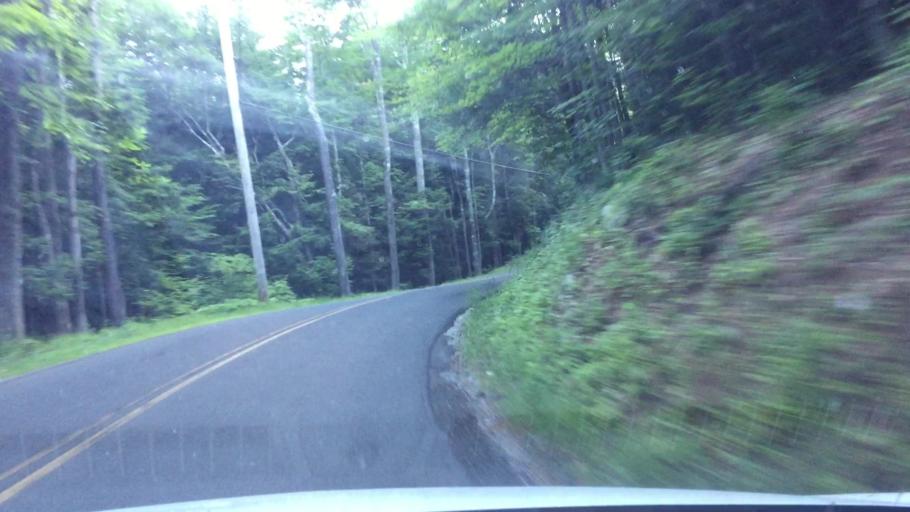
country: US
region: Massachusetts
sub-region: Berkshire County
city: Otis
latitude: 42.2401
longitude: -73.1140
